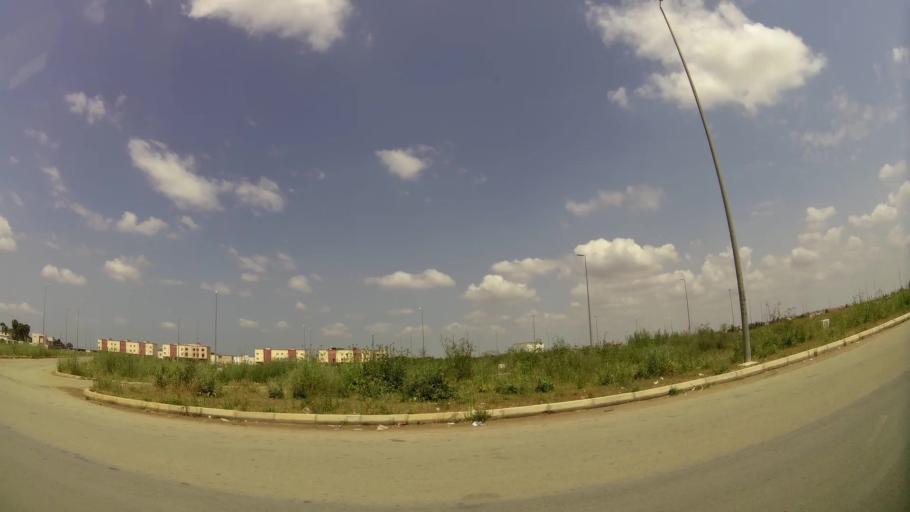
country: MA
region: Rabat-Sale-Zemmour-Zaer
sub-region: Khemisset
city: Tiflet
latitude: 34.0118
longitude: -6.5288
